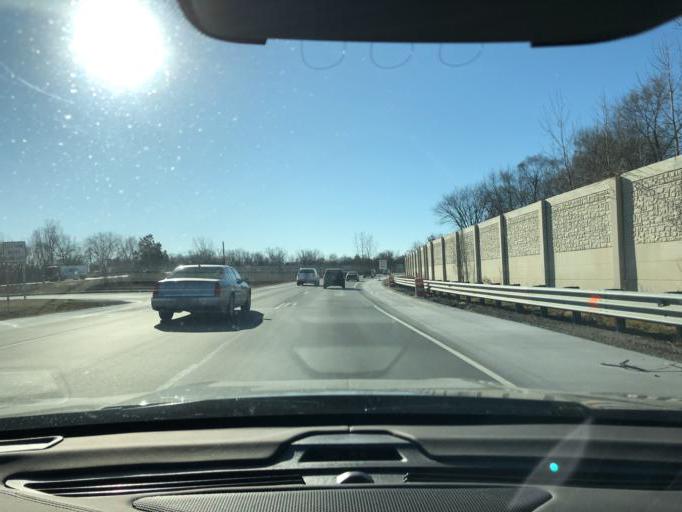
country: US
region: Michigan
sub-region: Washtenaw County
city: Ypsilanti
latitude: 42.2346
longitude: -83.5762
